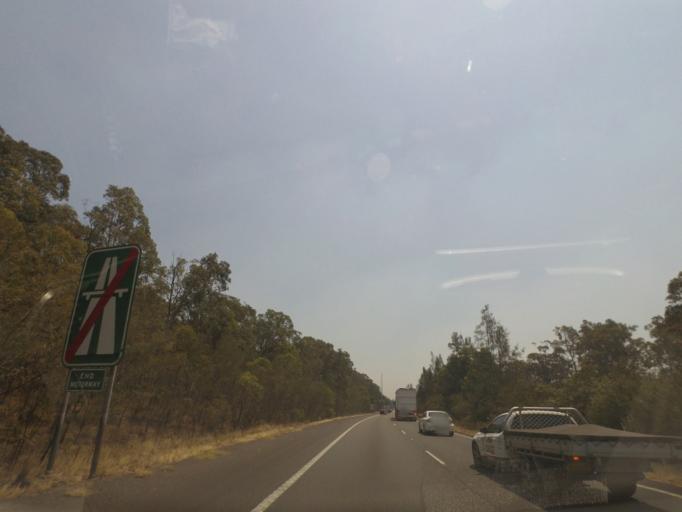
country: AU
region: New South Wales
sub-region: Newcastle
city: Beresfield
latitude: -32.8264
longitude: 151.6330
